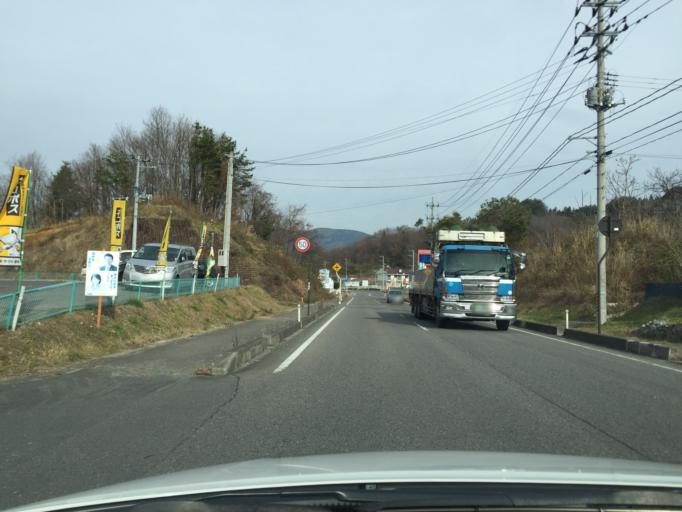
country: JP
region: Fukushima
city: Funehikimachi-funehiki
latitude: 37.4308
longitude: 140.5926
